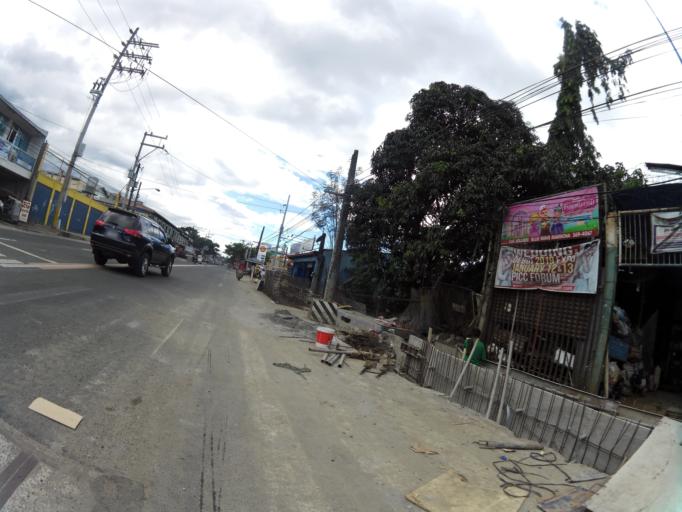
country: PH
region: Calabarzon
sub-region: Province of Rizal
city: Antipolo
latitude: 14.6331
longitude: 121.1113
